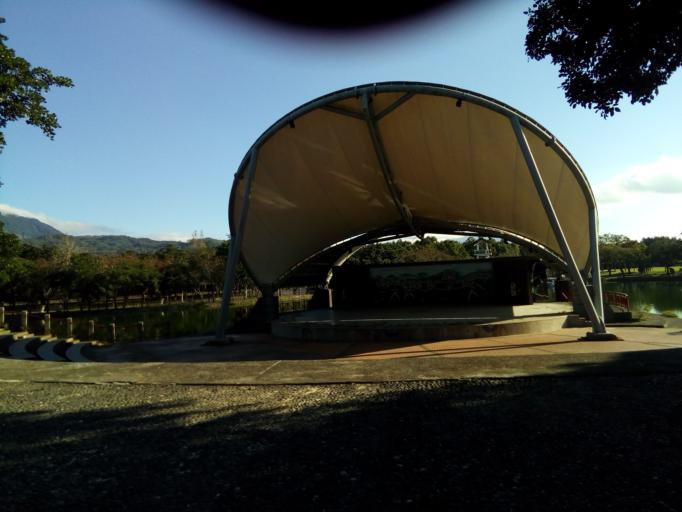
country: TW
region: Taiwan
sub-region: Taitung
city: Taitung
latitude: 23.0374
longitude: 121.1721
